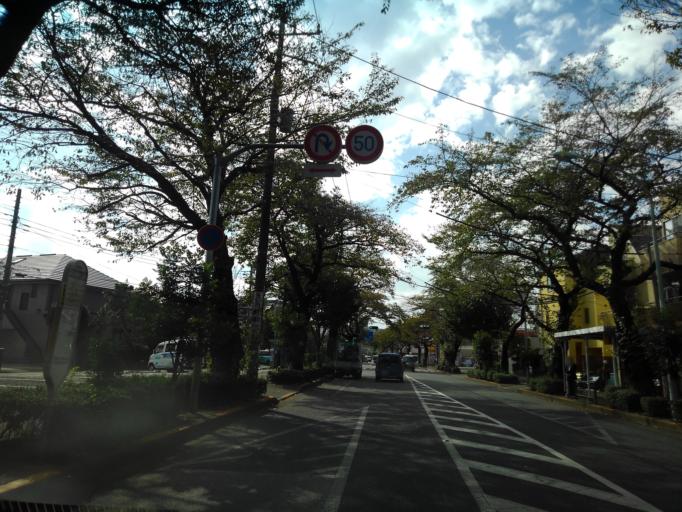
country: JP
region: Tokyo
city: Kokubunji
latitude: 35.6913
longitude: 139.4980
